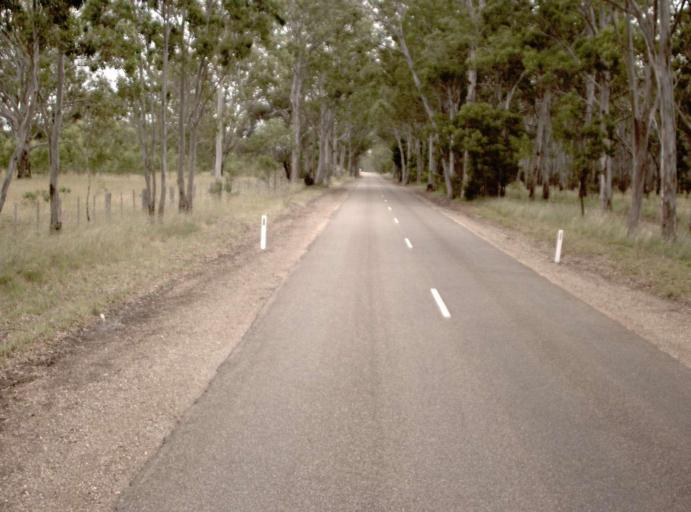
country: AU
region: Victoria
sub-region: Wellington
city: Sale
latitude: -37.8622
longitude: 147.0689
